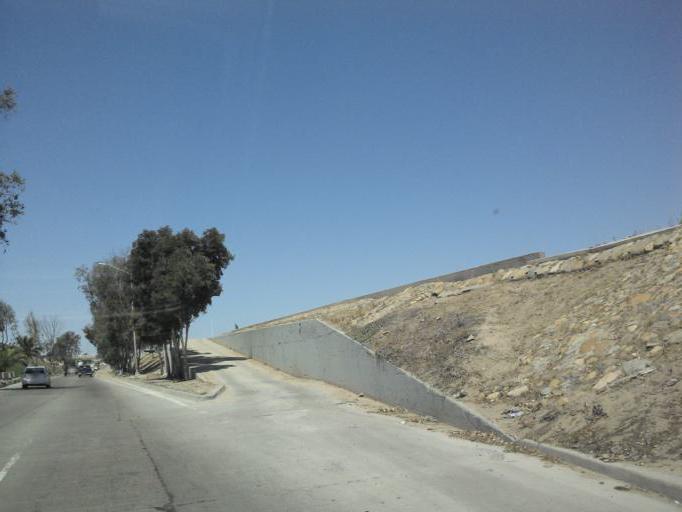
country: MX
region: Baja California
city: Tijuana
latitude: 32.5360
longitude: -117.0297
